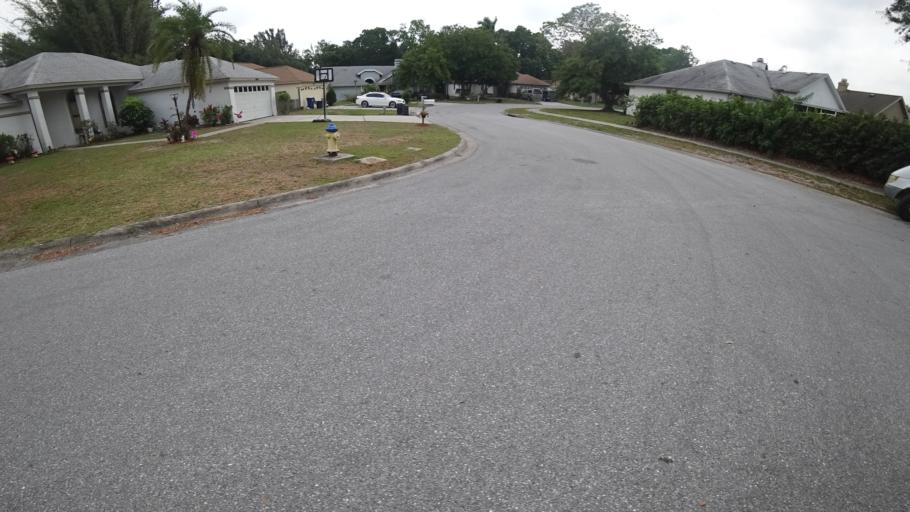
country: US
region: Florida
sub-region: Sarasota County
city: North Sarasota
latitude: 27.4051
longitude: -82.5154
